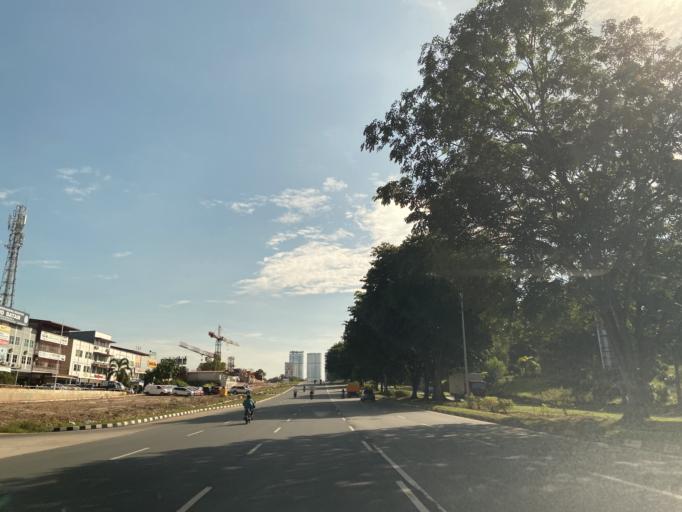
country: SG
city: Singapore
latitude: 1.1048
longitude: 104.0397
